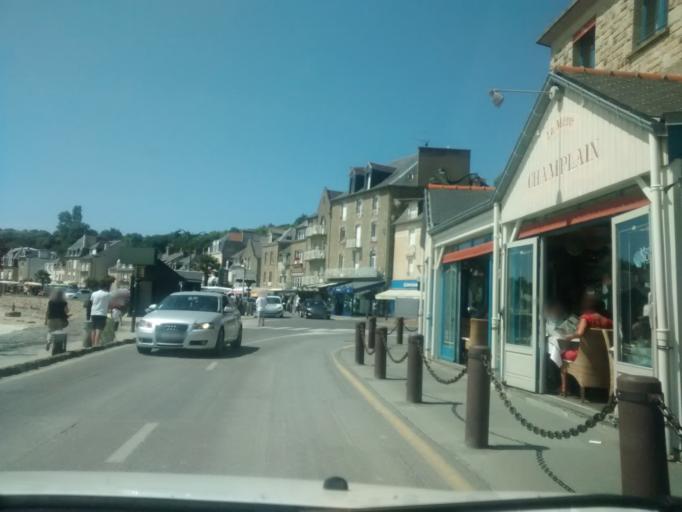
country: FR
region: Brittany
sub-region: Departement d'Ille-et-Vilaine
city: Cancale
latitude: 48.6710
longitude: -1.8525
